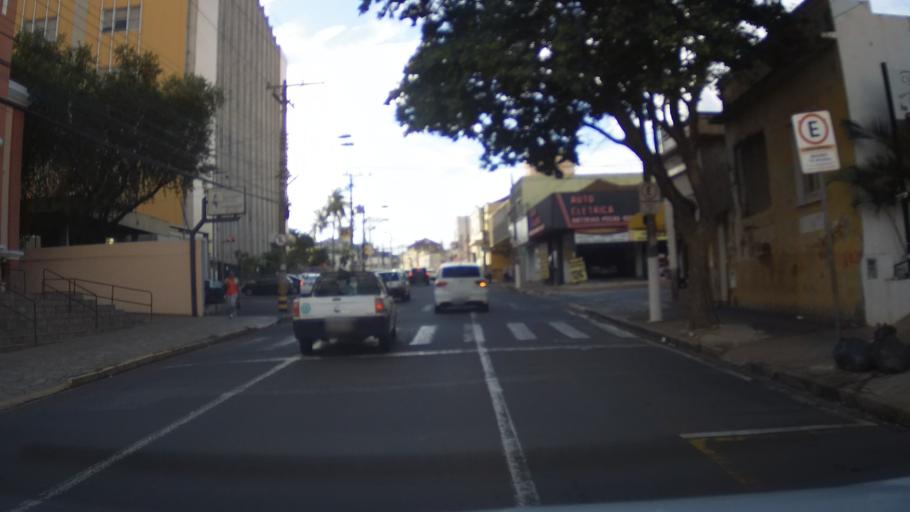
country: BR
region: Sao Paulo
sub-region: Campinas
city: Campinas
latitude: -22.9003
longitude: -47.0805
